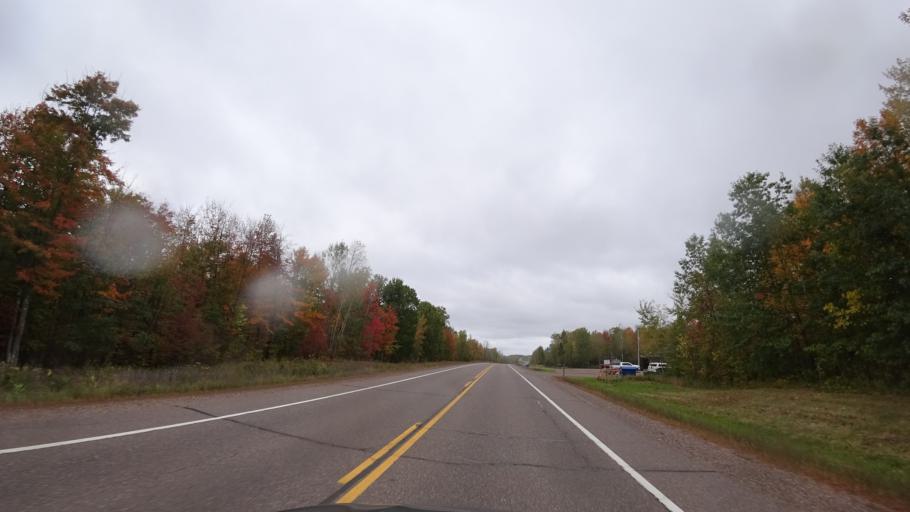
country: US
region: Wisconsin
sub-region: Rusk County
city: Ladysmith
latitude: 45.5774
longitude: -91.1120
